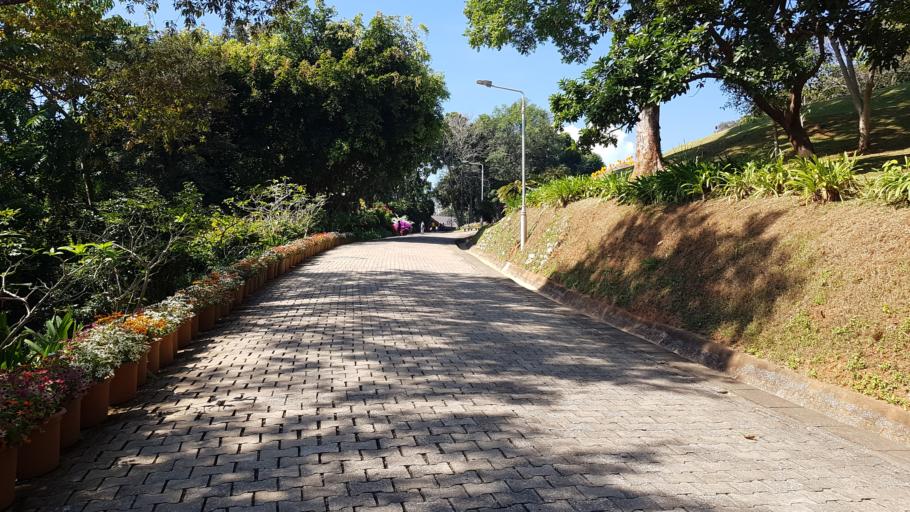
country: TH
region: Chiang Rai
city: Mae Fa Luang
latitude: 20.2868
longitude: 99.8109
